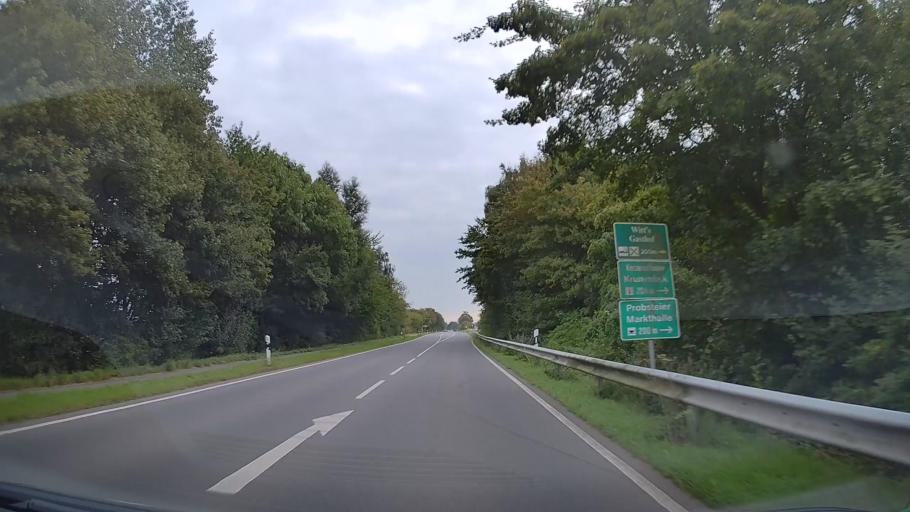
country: DE
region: Schleswig-Holstein
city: Stakendorf
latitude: 54.3865
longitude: 10.4374
